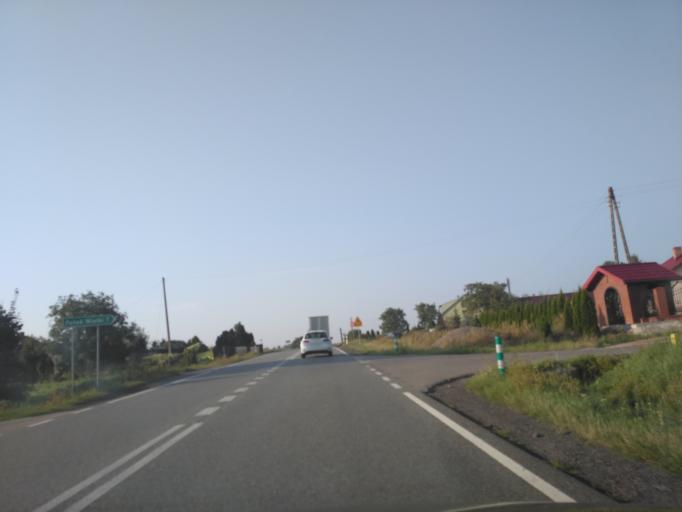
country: PL
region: Lublin Voivodeship
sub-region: Powiat janowski
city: Modliborzyce
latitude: 50.7962
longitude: 22.3183
